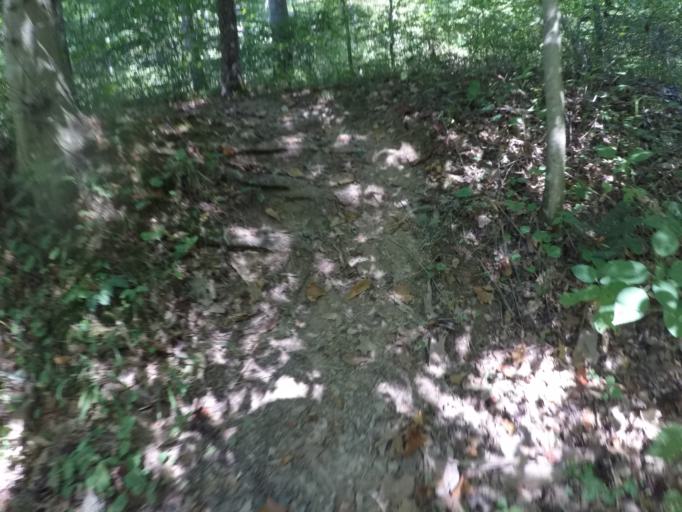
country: US
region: Ohio
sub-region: Lawrence County
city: Ironton
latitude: 38.6244
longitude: -82.6195
